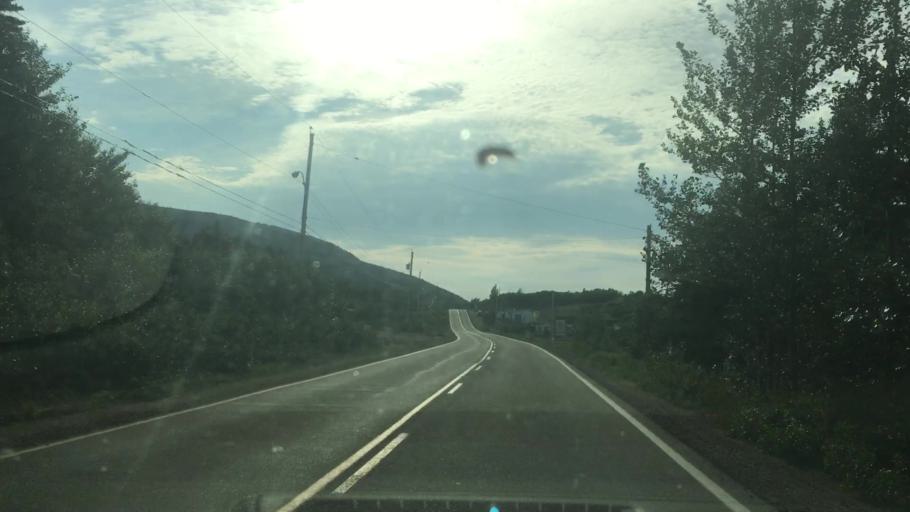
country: CA
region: Nova Scotia
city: Sydney Mines
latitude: 46.8248
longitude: -60.8149
